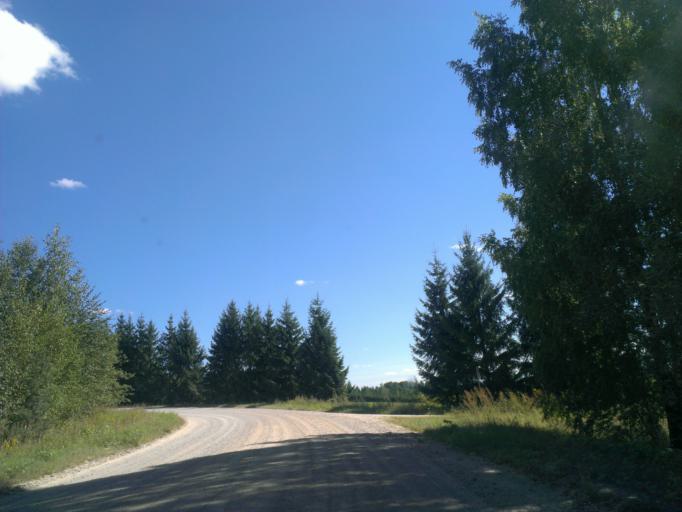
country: LV
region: Malpils
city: Malpils
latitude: 57.0063
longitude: 24.9687
